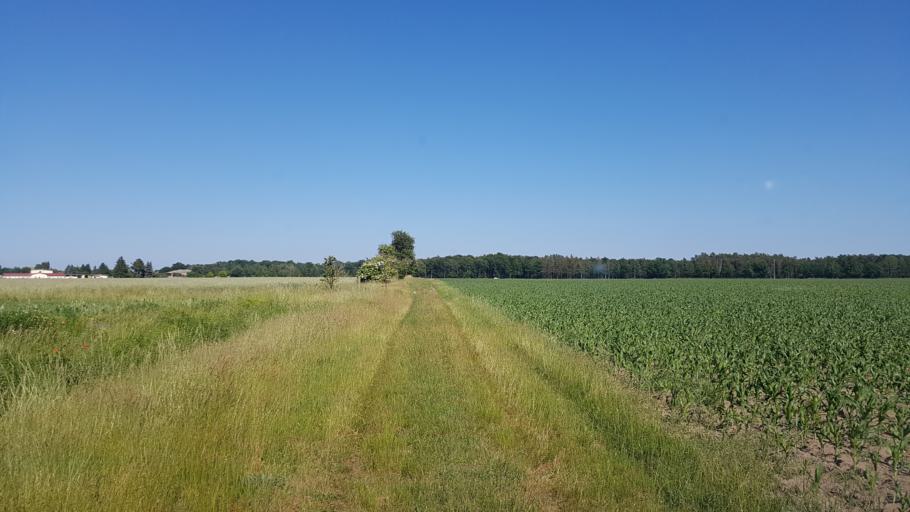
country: DE
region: Brandenburg
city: Sonnewalde
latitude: 51.6842
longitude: 13.6754
